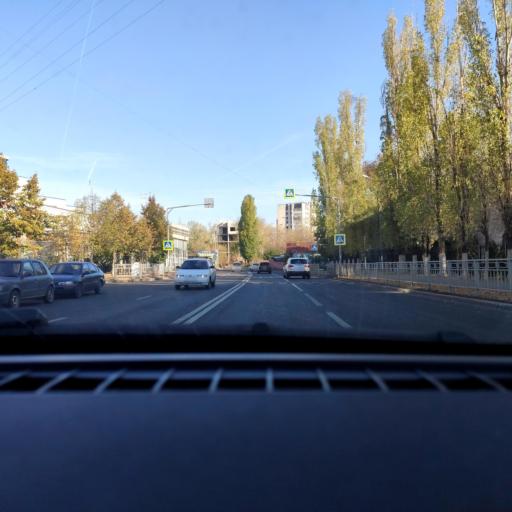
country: RU
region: Voronezj
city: Voronezh
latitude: 51.6735
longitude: 39.2570
